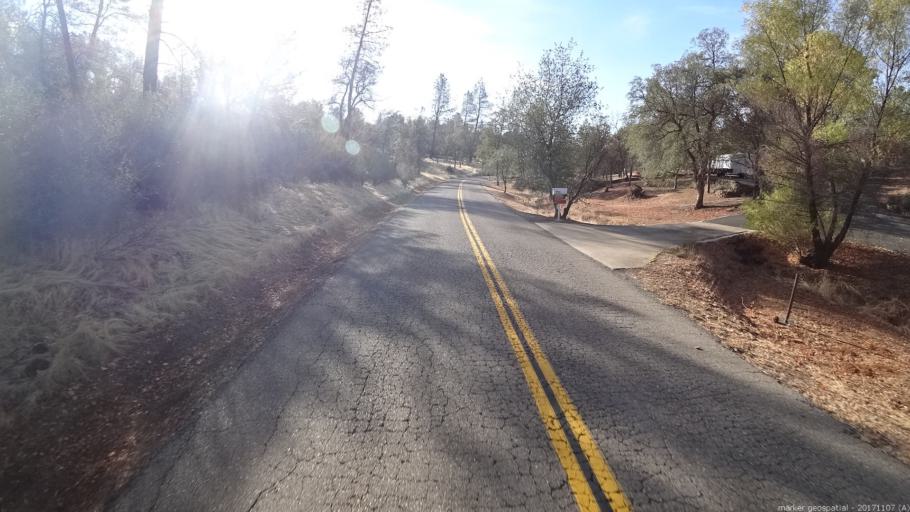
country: US
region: California
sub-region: Shasta County
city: Shasta
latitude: 40.5451
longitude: -122.4550
